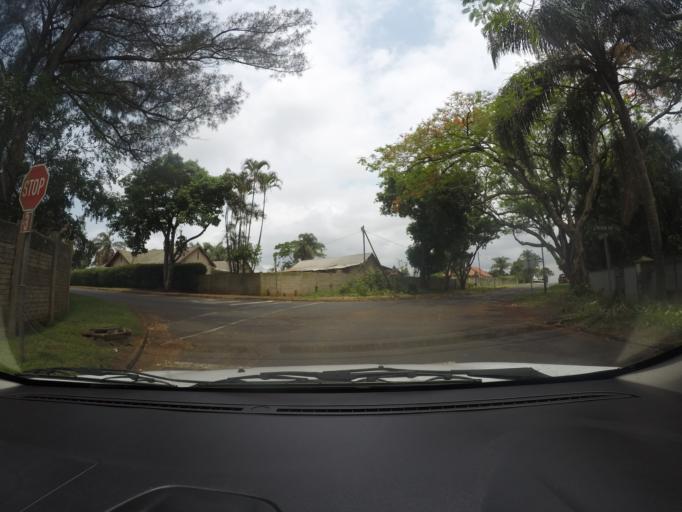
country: ZA
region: KwaZulu-Natal
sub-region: uThungulu District Municipality
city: Empangeni
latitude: -28.7509
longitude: 31.8935
